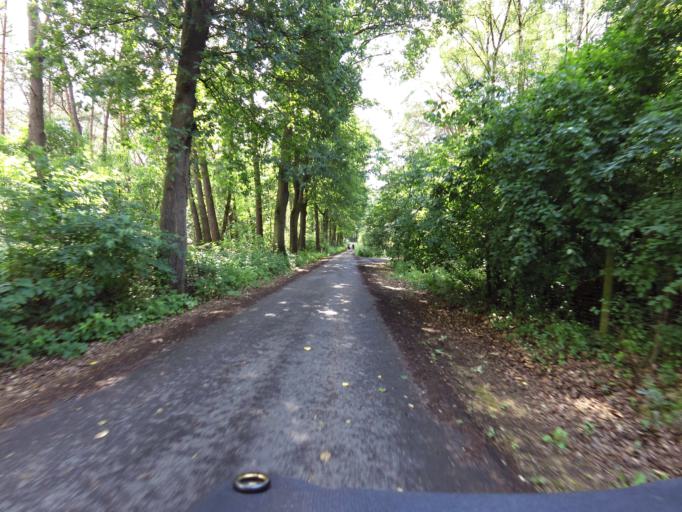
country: DE
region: North Rhine-Westphalia
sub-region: Regierungsbezirk Dusseldorf
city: Niederkruchten
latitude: 51.1813
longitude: 6.1965
